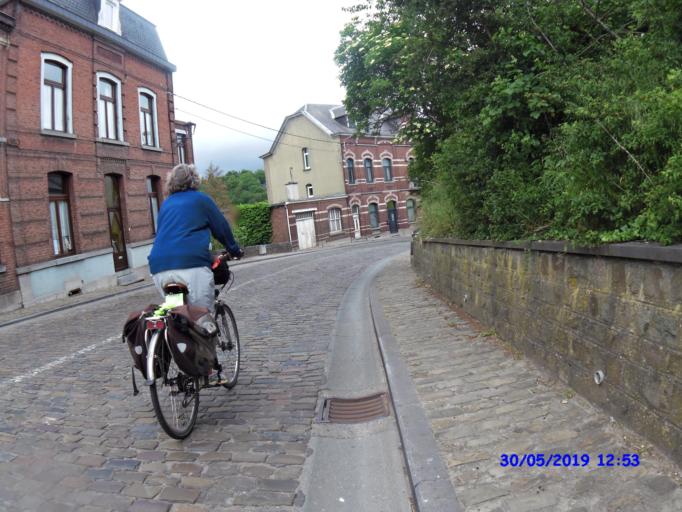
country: BE
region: Wallonia
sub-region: Province du Hainaut
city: Thuin
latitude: 50.3403
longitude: 4.2830
